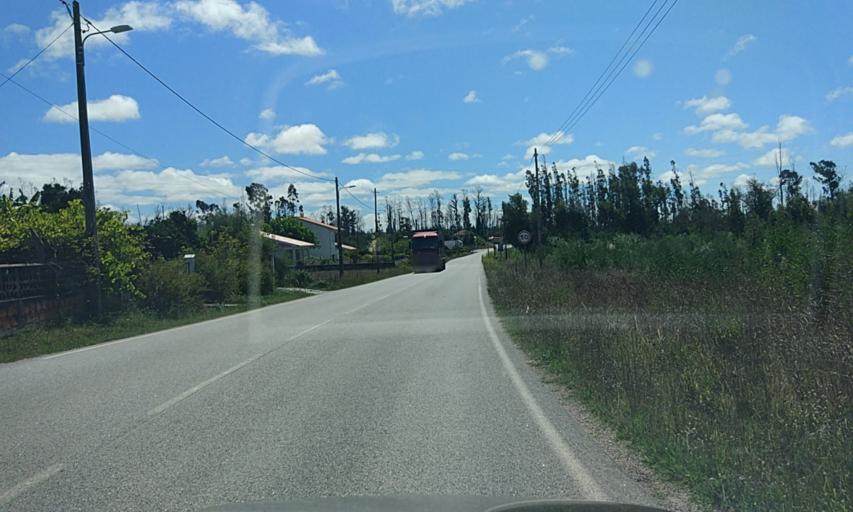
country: PT
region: Coimbra
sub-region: Mira
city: Mira
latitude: 40.4098
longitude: -8.7353
